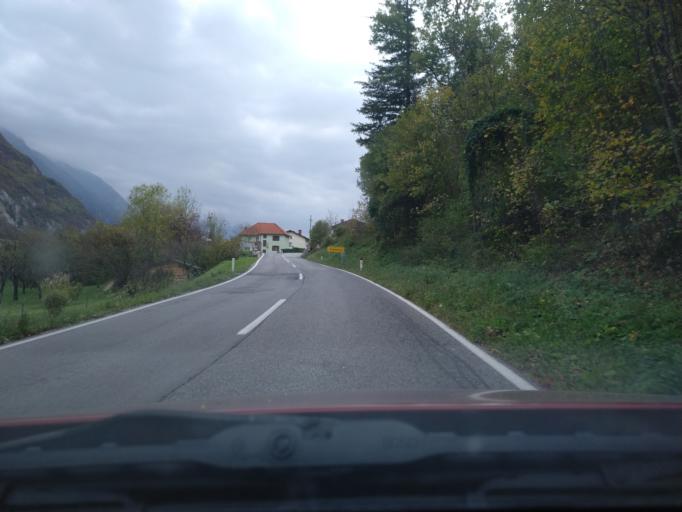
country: SI
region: Bovec
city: Bovec
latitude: 46.2929
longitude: 13.4958
